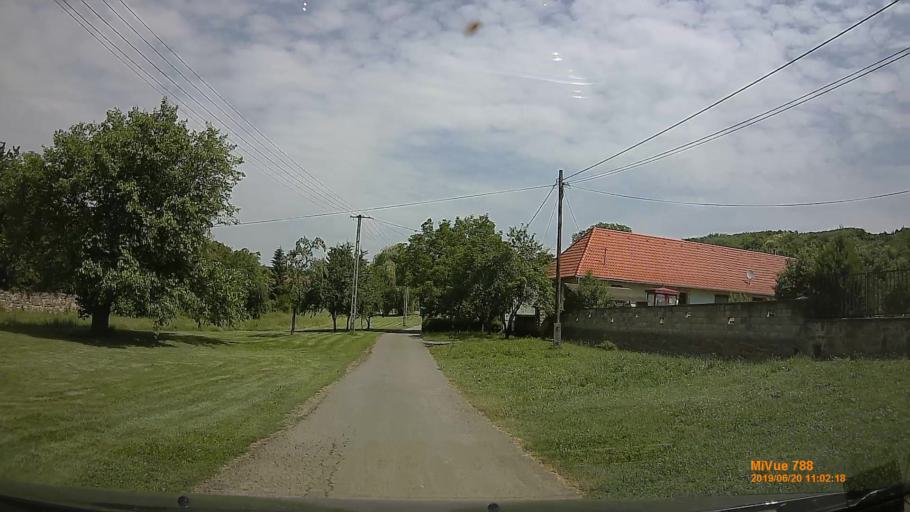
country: HU
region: Baranya
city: Mecseknadasd
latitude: 46.1783
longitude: 18.5115
